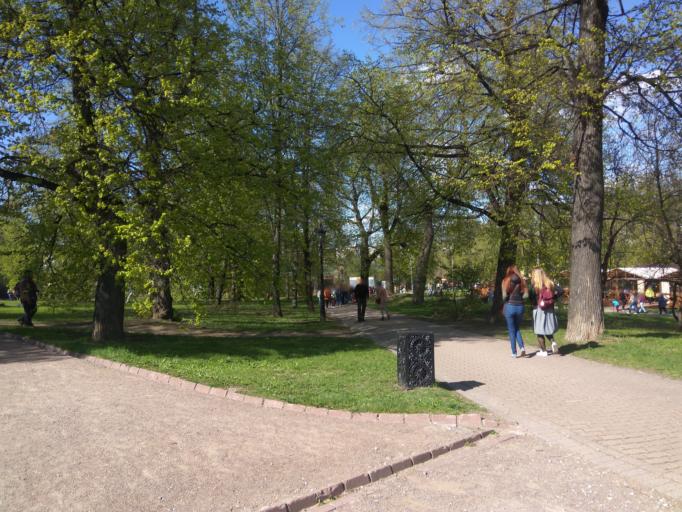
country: RU
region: Moscow
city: Kolomenskoye
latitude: 55.6696
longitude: 37.6714
